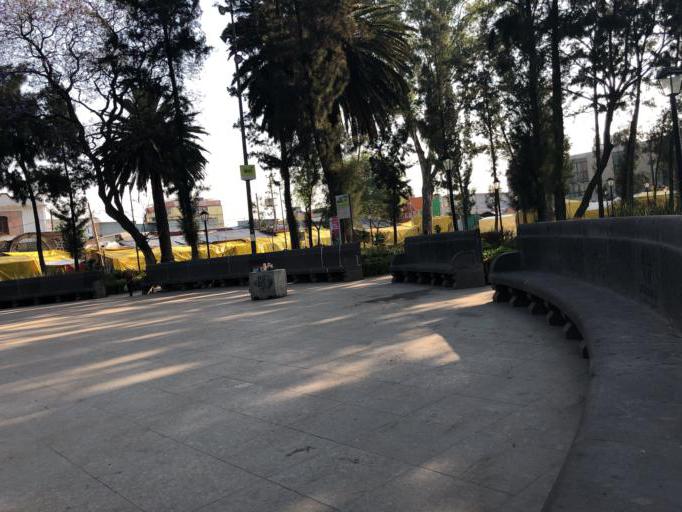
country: MX
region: Mexico City
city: Iztapalapa
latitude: 19.3598
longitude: -99.0923
